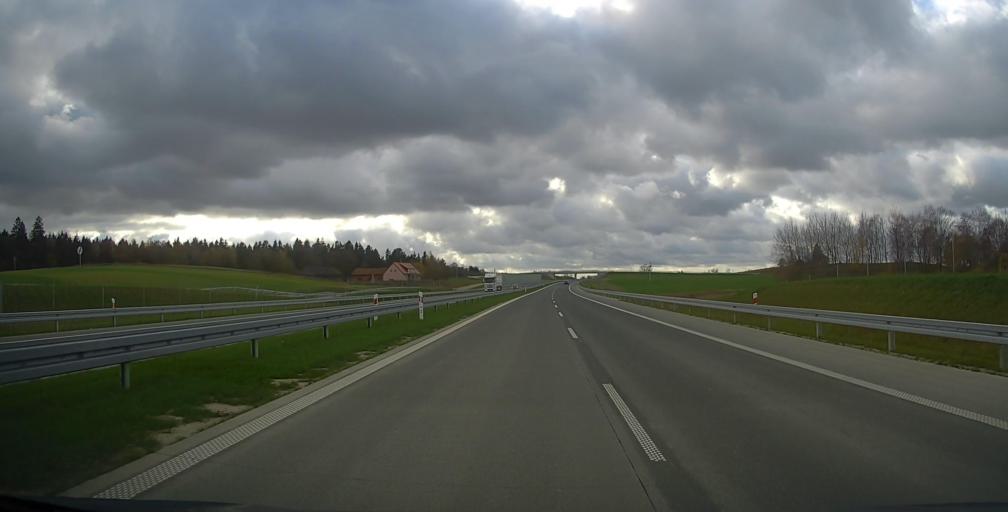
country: PL
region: Podlasie
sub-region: Powiat suwalski
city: Raczki
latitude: 53.9289
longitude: 22.7554
